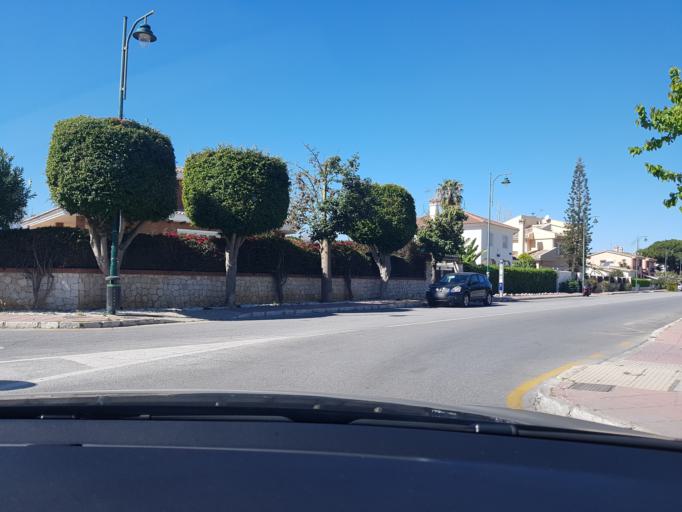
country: ES
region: Andalusia
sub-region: Provincia de Malaga
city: Torremolinos
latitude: 36.6676
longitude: -4.4611
